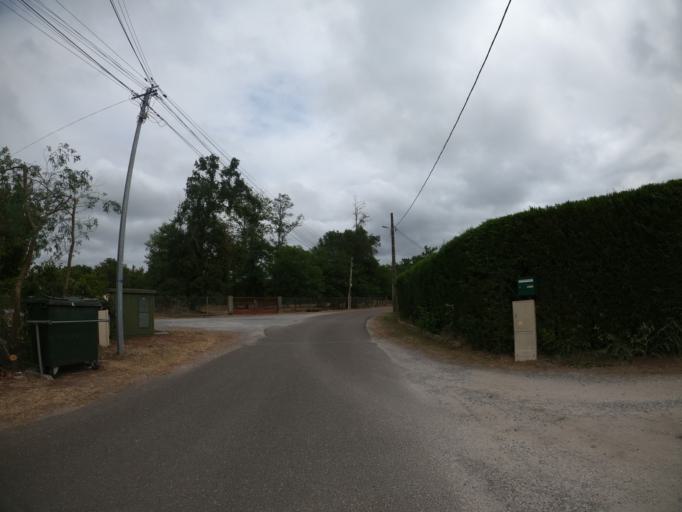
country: FR
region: Aquitaine
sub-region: Departement des Landes
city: Leon
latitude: 43.8849
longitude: -1.3029
